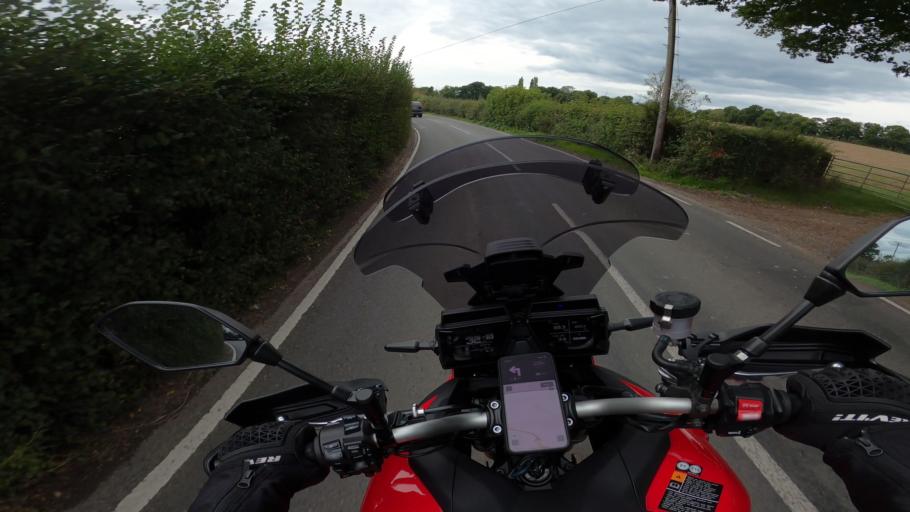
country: GB
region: England
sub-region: Surrey
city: Lingfield
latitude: 51.1900
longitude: 0.0098
